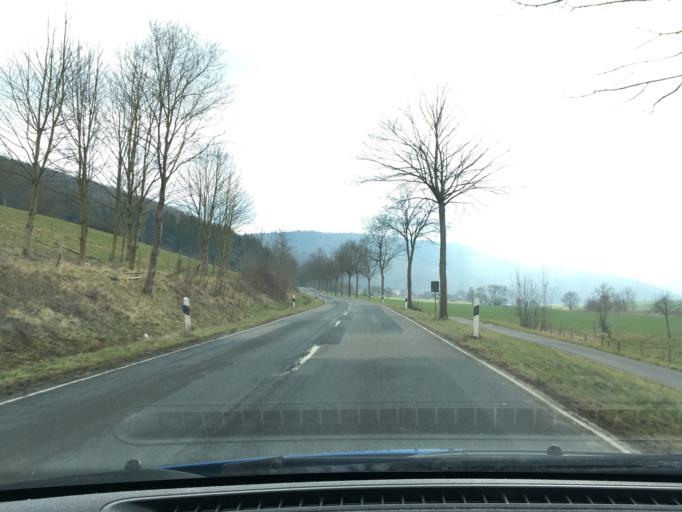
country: DE
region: Lower Saxony
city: Buhren
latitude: 51.5366
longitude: 9.6246
